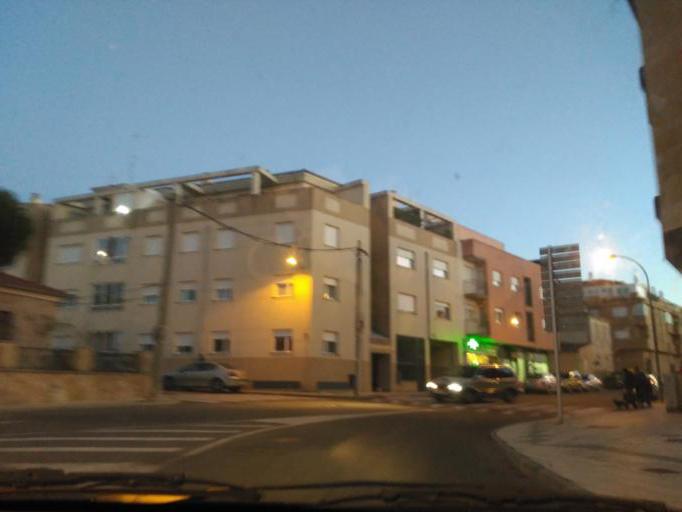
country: ES
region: Castille and Leon
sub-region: Provincia de Salamanca
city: Villares de la Reina
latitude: 41.0077
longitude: -5.6495
